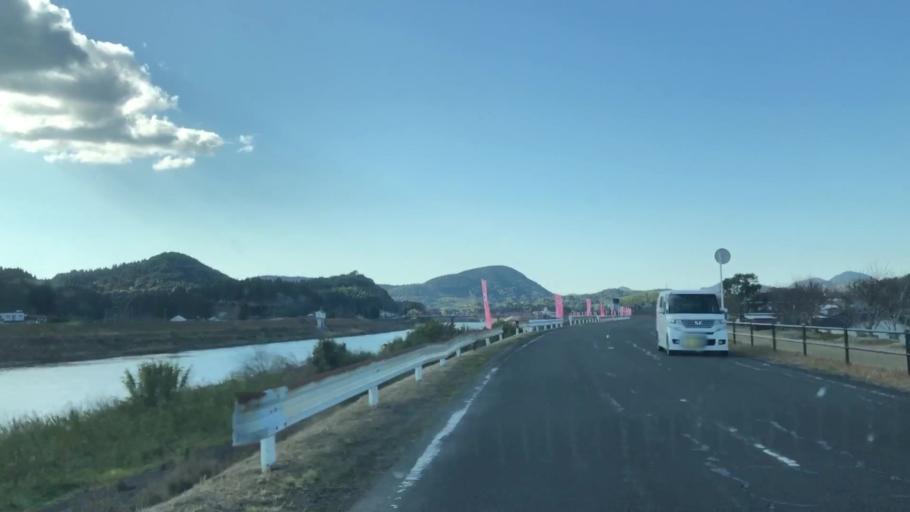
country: JP
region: Kagoshima
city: Satsumasendai
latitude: 31.8595
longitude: 130.3460
